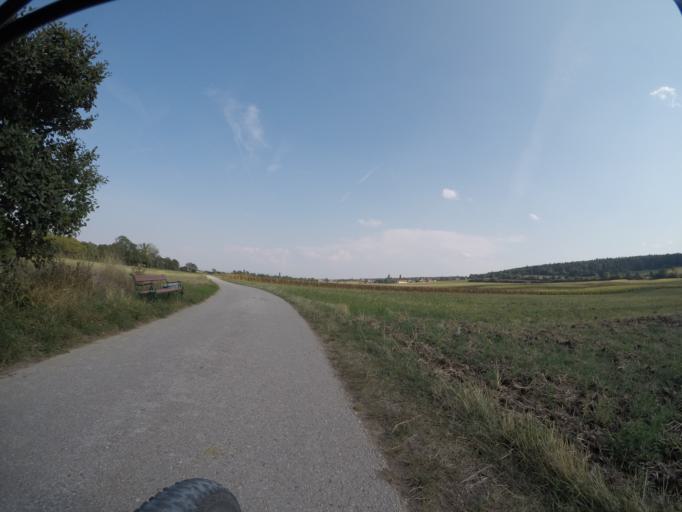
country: AT
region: Lower Austria
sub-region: Politischer Bezirk Baden
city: Hirtenberg
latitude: 47.9629
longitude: 16.1557
